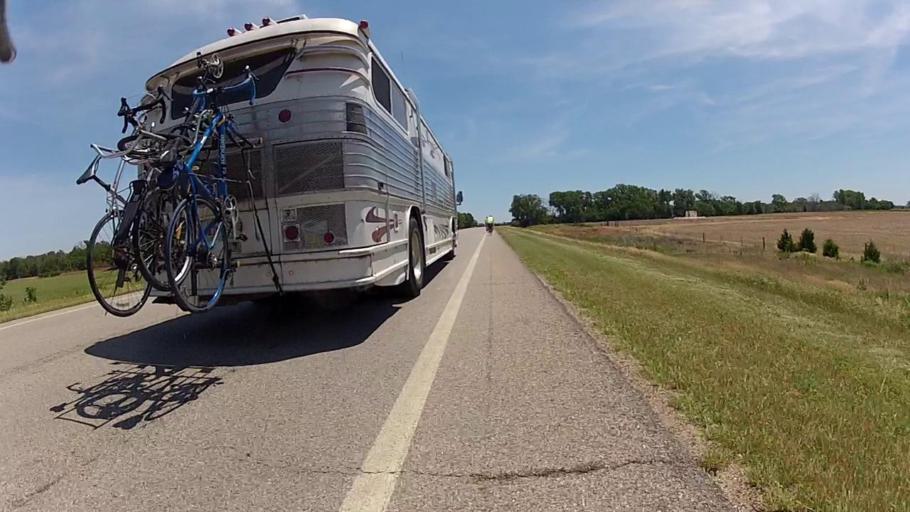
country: US
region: Kansas
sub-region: Barber County
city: Medicine Lodge
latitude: 37.2534
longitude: -98.4569
